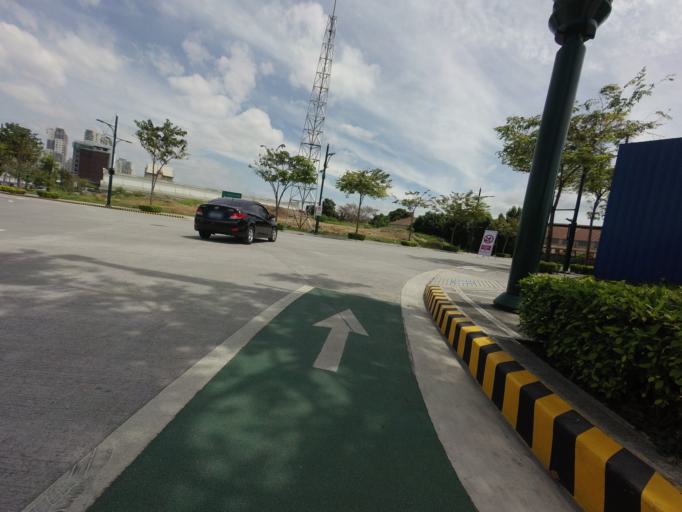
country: PH
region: Metro Manila
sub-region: Pasig
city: Pasig City
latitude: 14.5773
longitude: 121.0762
